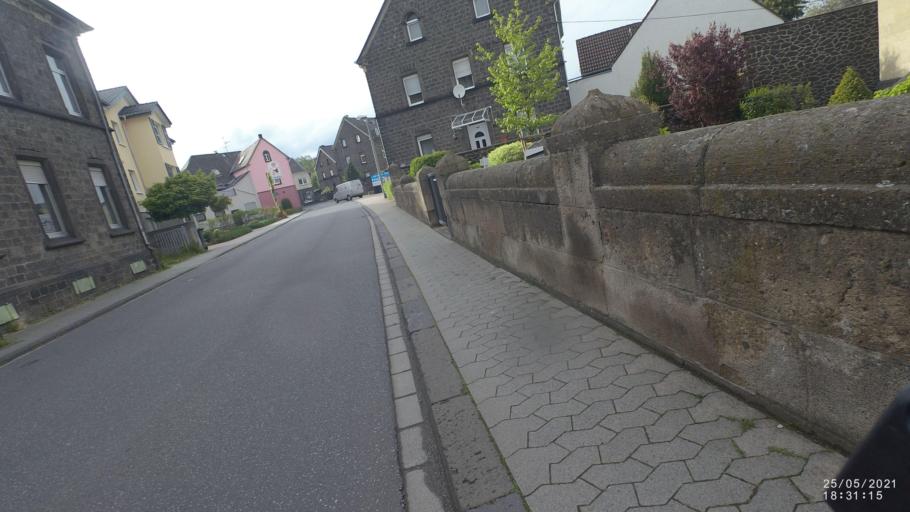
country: DE
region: Rheinland-Pfalz
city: Kottenheim
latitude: 50.3469
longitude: 7.2573
